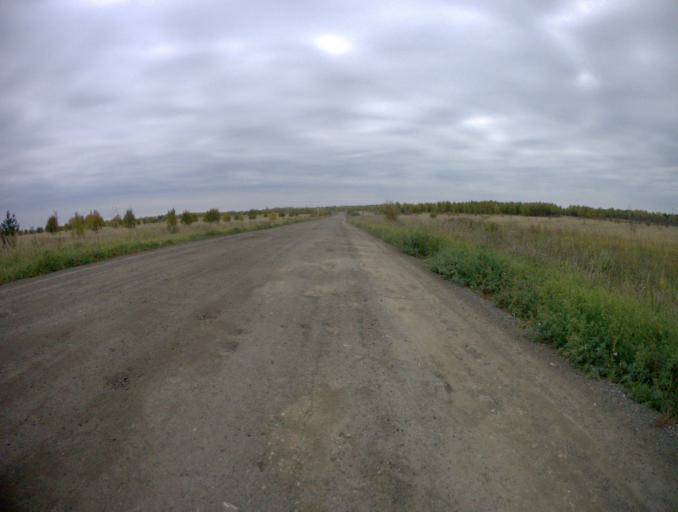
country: RU
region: Vladimir
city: Mstera
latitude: 56.3800
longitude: 41.8889
